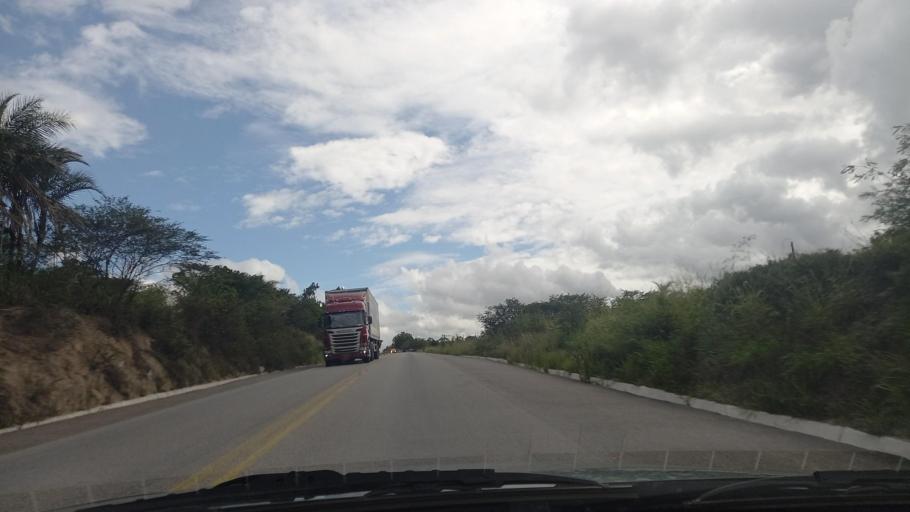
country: BR
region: Pernambuco
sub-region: Lajedo
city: Lajedo
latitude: -8.6759
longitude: -36.4012
